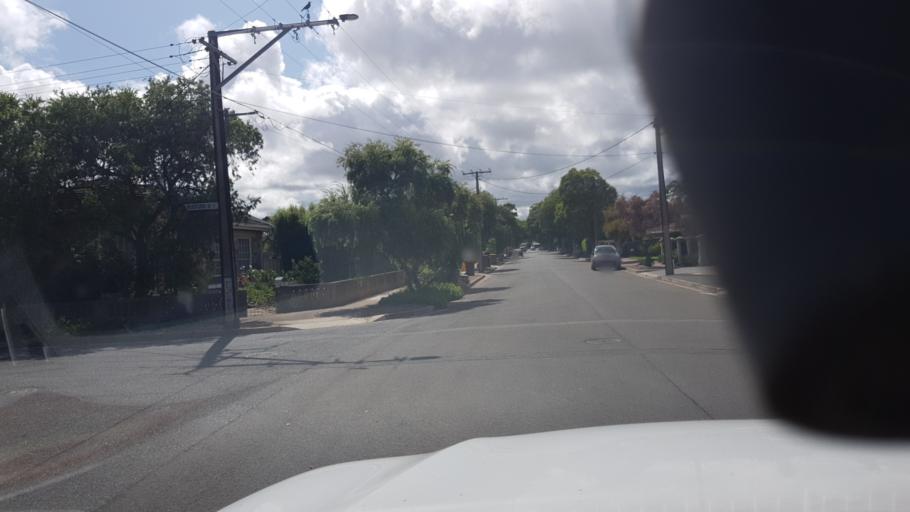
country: AU
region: South Australia
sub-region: Adelaide
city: Brighton
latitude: -35.0230
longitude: 138.5283
